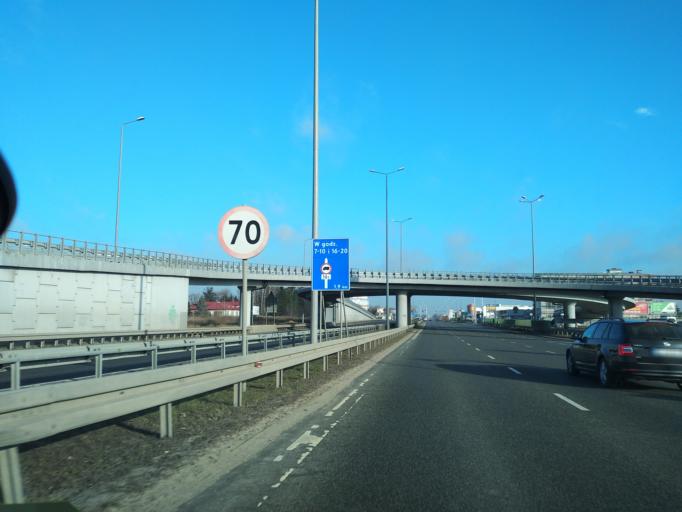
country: PL
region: Masovian Voivodeship
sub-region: Powiat piaseczynski
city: Mysiadlo
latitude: 52.0946
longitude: 21.0190
